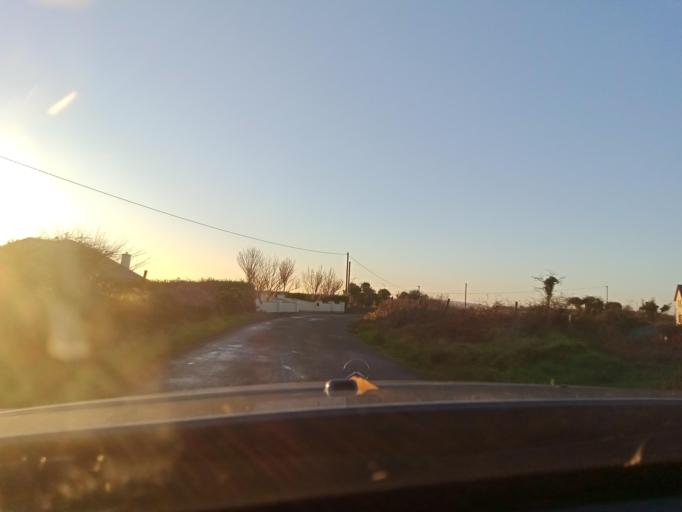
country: IE
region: Munster
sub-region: Waterford
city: Waterford
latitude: 52.3665
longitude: -7.1154
